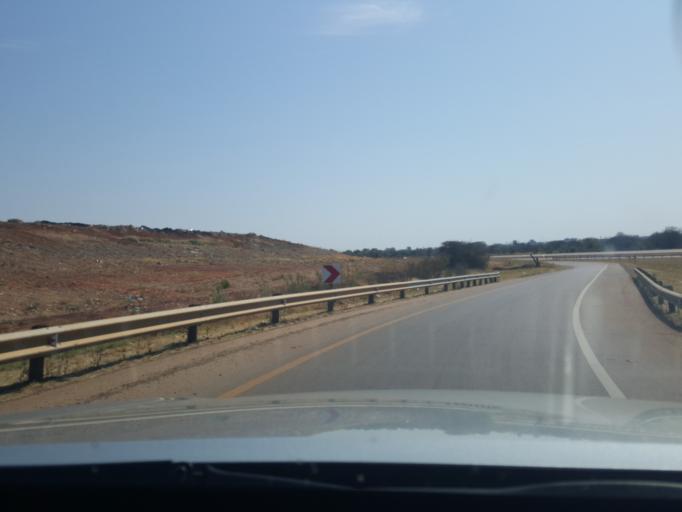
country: ZA
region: Gauteng
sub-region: City of Tshwane Metropolitan Municipality
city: Pretoria
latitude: -25.6484
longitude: 28.1521
